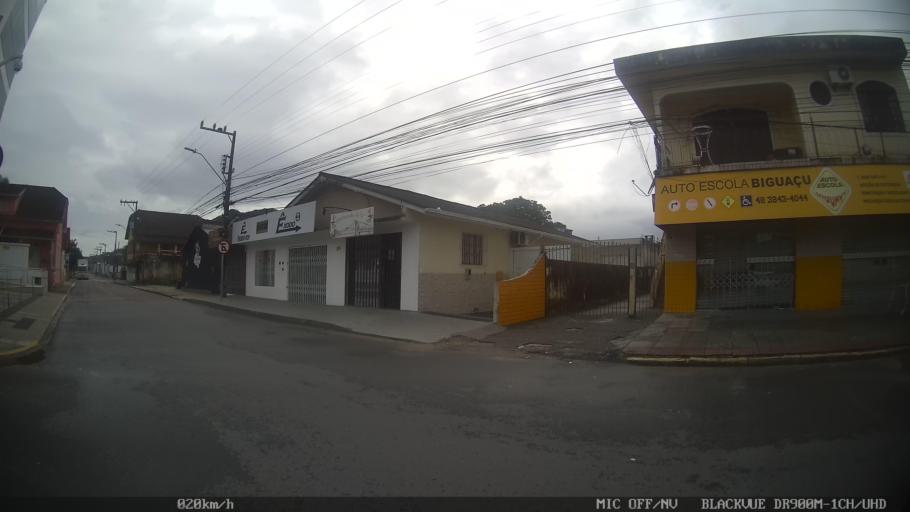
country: BR
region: Santa Catarina
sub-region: Biguacu
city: Biguacu
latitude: -27.4931
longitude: -48.6541
